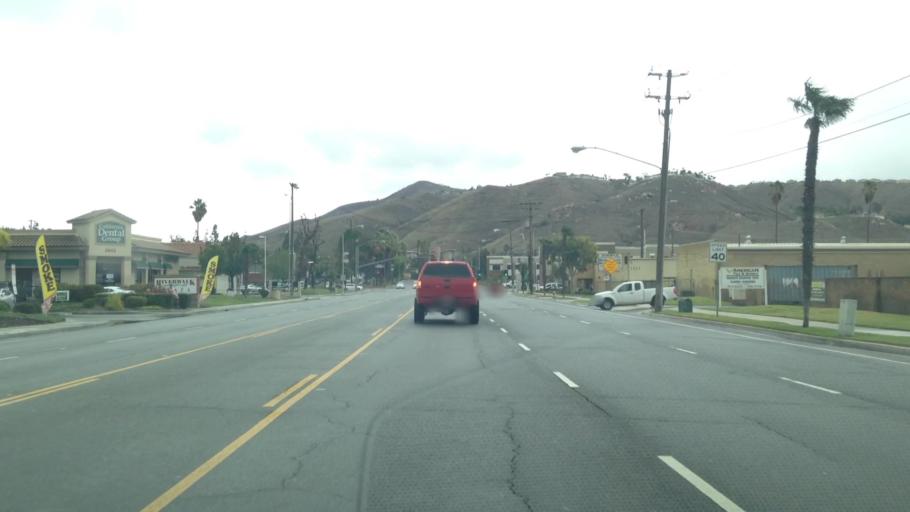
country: US
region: California
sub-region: Riverside County
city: Home Gardens
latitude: 33.8967
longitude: -117.4925
